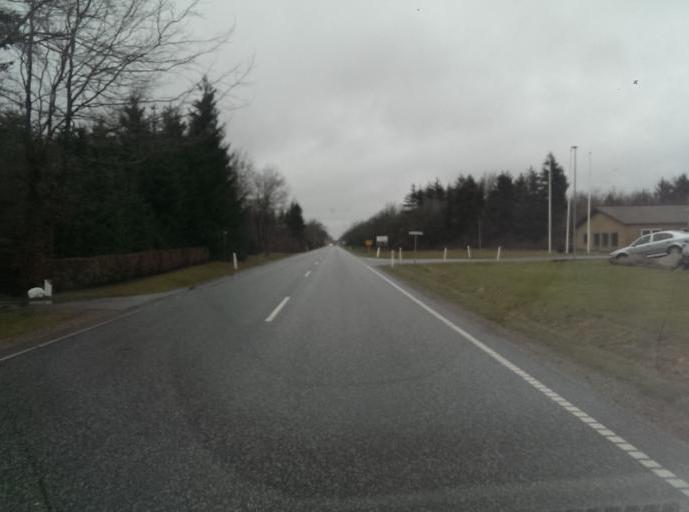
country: DK
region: Central Jutland
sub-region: Holstebro Kommune
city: Ulfborg
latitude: 56.2634
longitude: 8.3181
